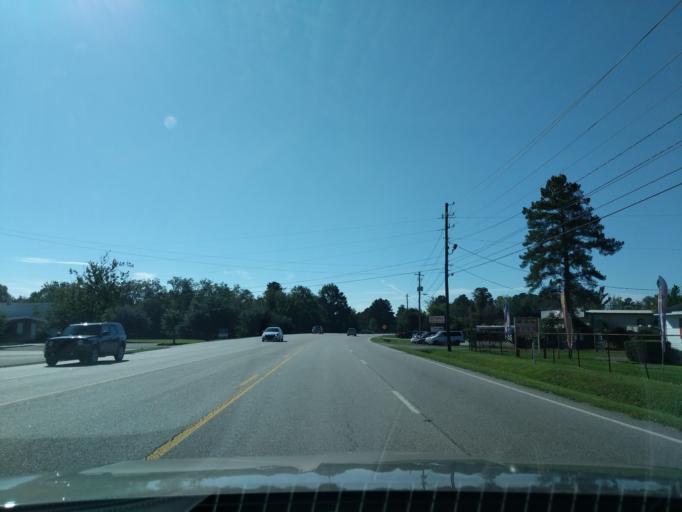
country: US
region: Georgia
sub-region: Richmond County
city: Augusta
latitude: 33.4252
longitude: -82.0062
